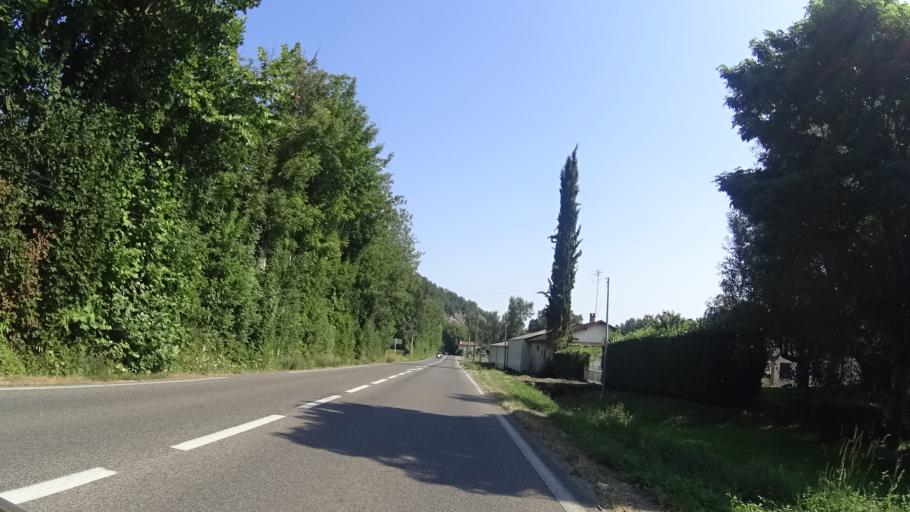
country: FR
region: Midi-Pyrenees
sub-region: Departement de l'Ariege
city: Lavelanet
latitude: 42.9518
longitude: 1.8600
